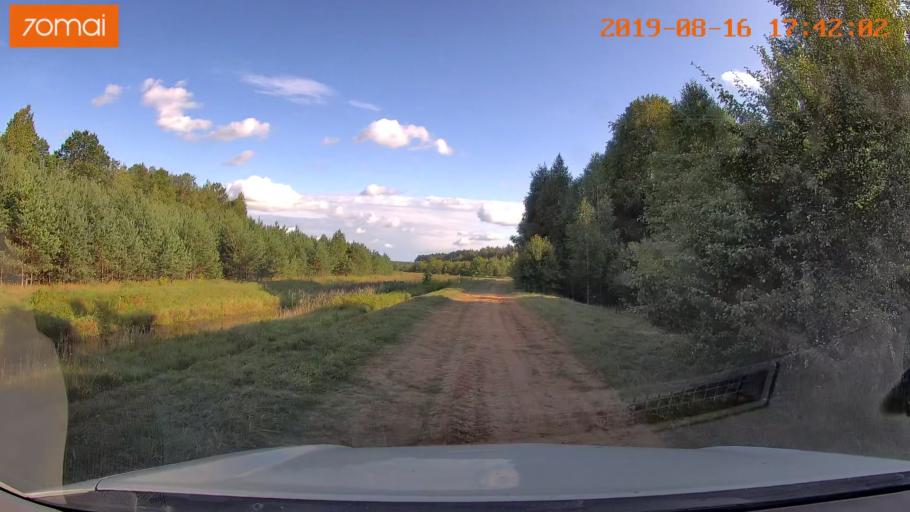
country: BY
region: Mogilev
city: Asipovichy
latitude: 53.2381
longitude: 28.6650
